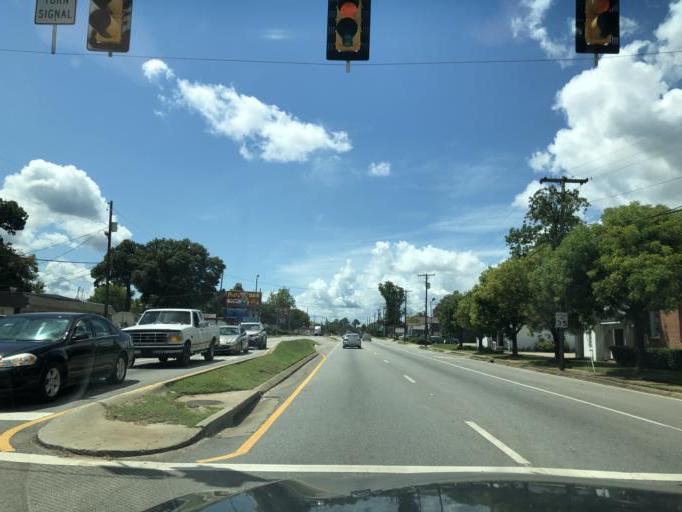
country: US
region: Alabama
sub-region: Barbour County
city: Eufaula
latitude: 31.8882
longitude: -85.1455
